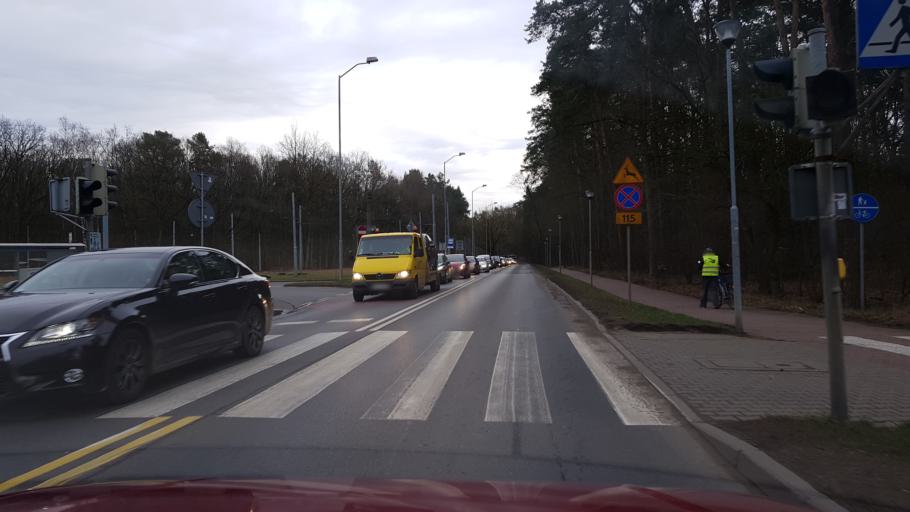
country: PL
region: West Pomeranian Voivodeship
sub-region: Szczecin
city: Szczecin
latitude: 53.4716
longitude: 14.4862
